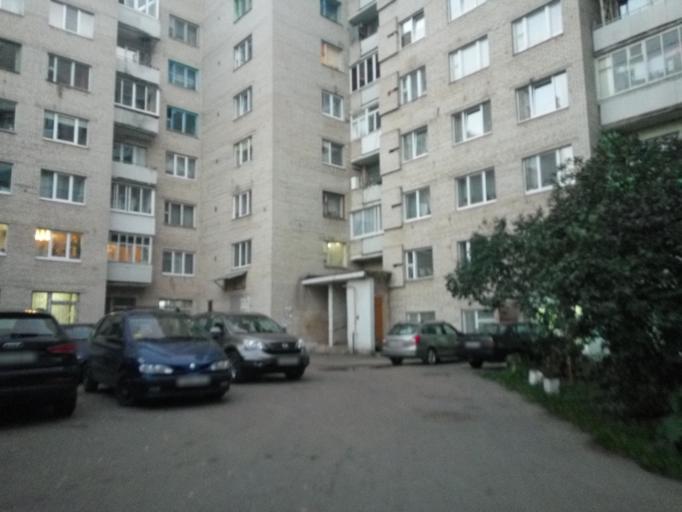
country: BY
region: Vitebsk
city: Vitebsk
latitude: 55.2003
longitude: 30.2402
